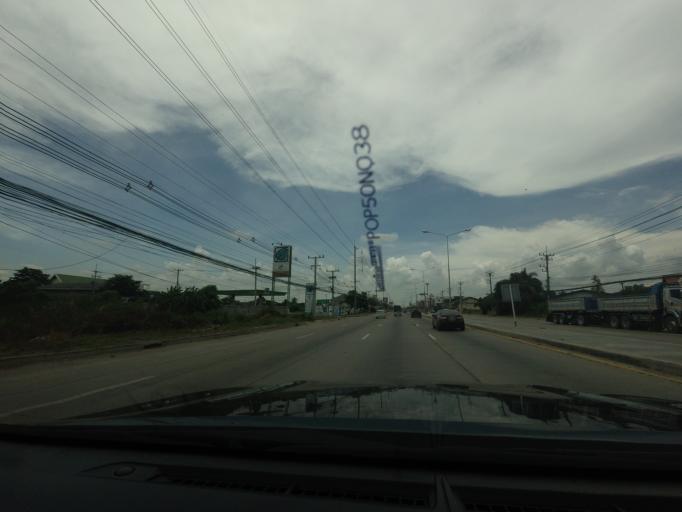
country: TH
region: Nakhon Pathom
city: Nakhon Pathom
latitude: 13.8496
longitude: 100.0201
